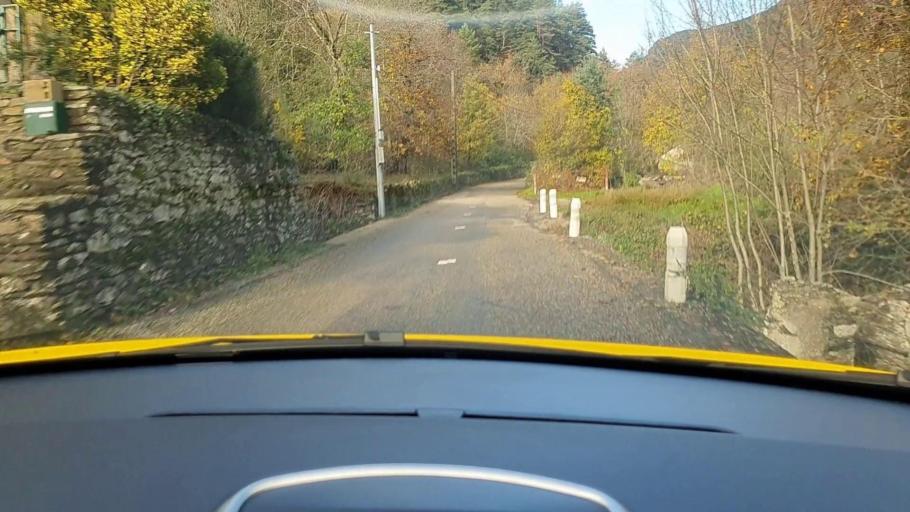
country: FR
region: Languedoc-Roussillon
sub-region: Departement du Gard
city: Valleraugue
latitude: 44.1595
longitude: 3.6755
